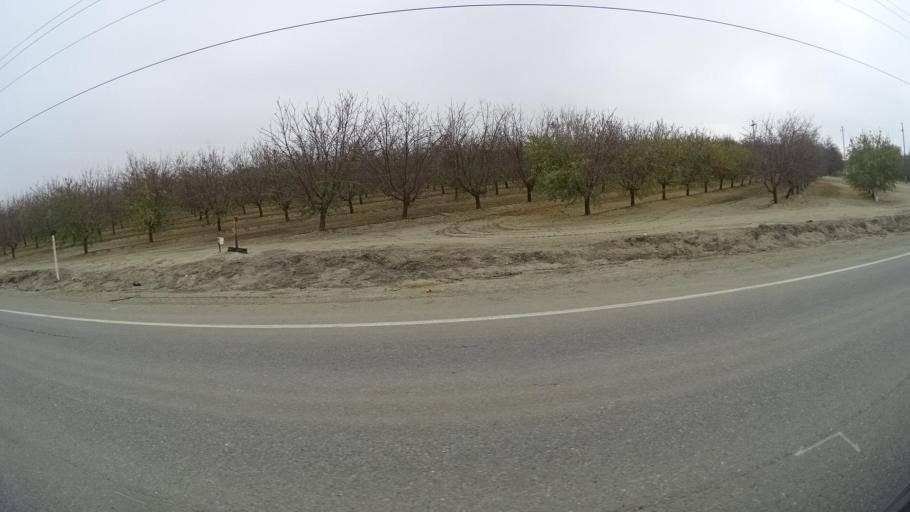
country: US
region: California
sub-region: Kern County
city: Greenfield
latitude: 35.0850
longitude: -119.1183
